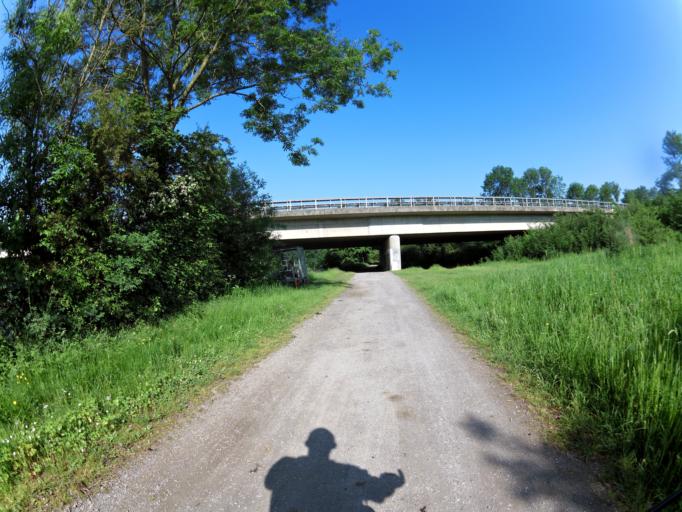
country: DE
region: North Rhine-Westphalia
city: Julich
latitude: 50.9382
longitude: 6.3433
